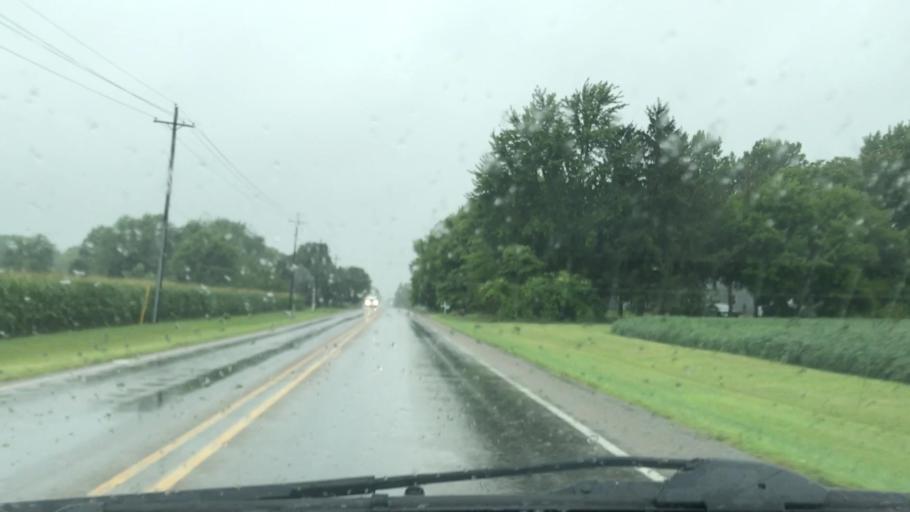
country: US
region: Indiana
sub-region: Hamilton County
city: Sheridan
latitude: 40.1156
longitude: -86.1768
